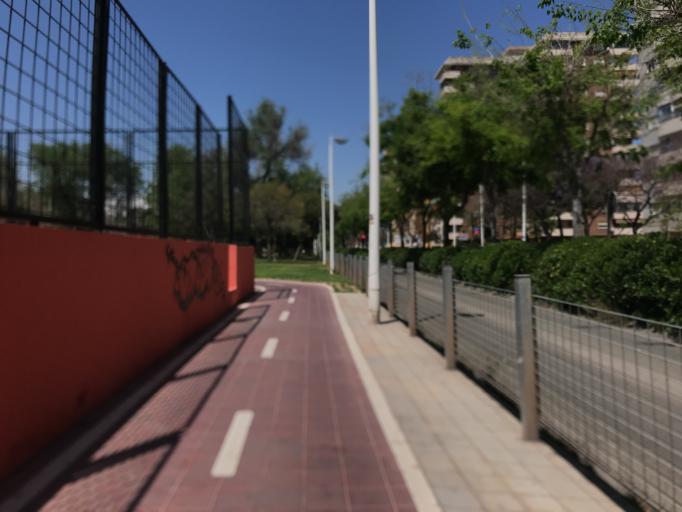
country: ES
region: Valencia
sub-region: Provincia de Valencia
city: Mislata
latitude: 39.4646
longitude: -0.4056
